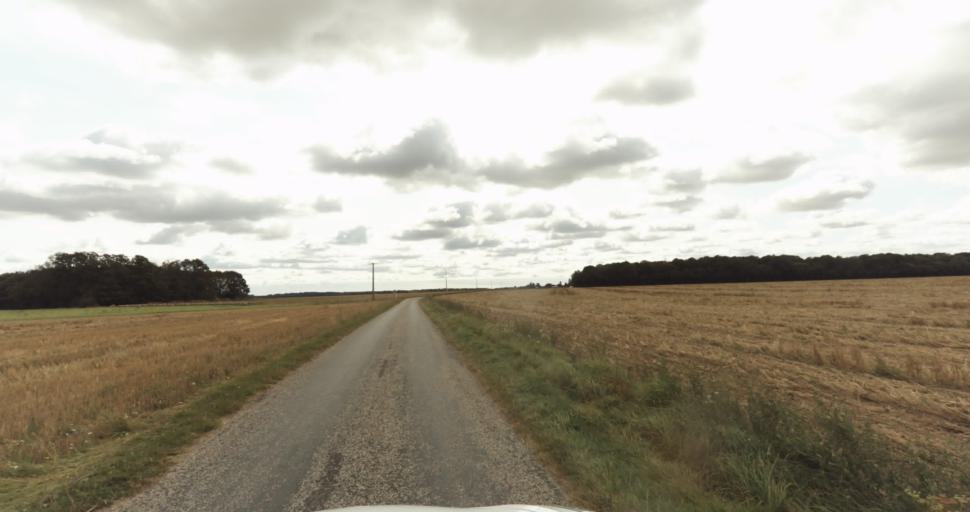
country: FR
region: Haute-Normandie
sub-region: Departement de l'Eure
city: Nonancourt
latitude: 48.7935
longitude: 1.1398
